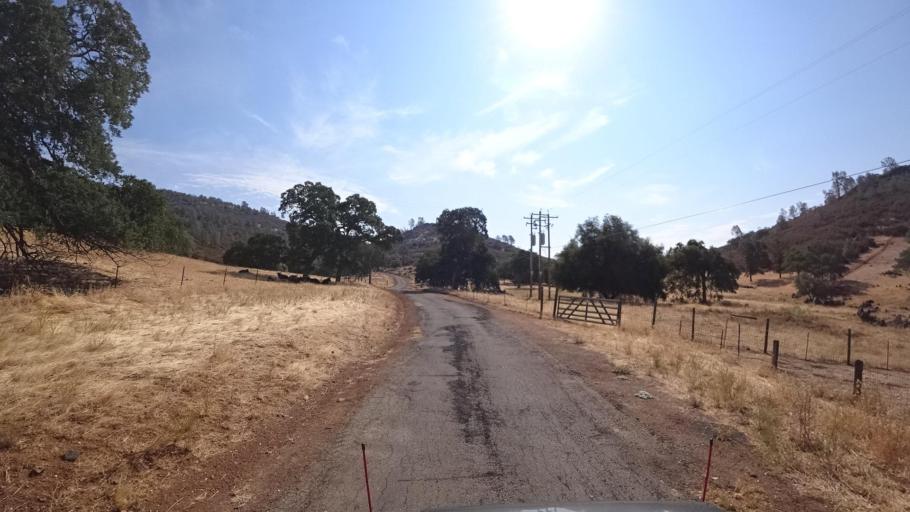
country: US
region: California
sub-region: Tuolumne County
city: Tuolumne City
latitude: 37.7244
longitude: -120.2586
